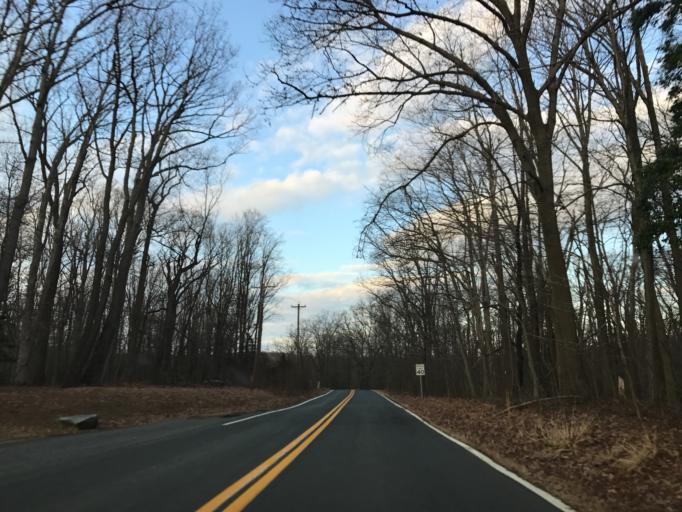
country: US
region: Maryland
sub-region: Cecil County
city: Charlestown
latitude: 39.4841
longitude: -75.9821
